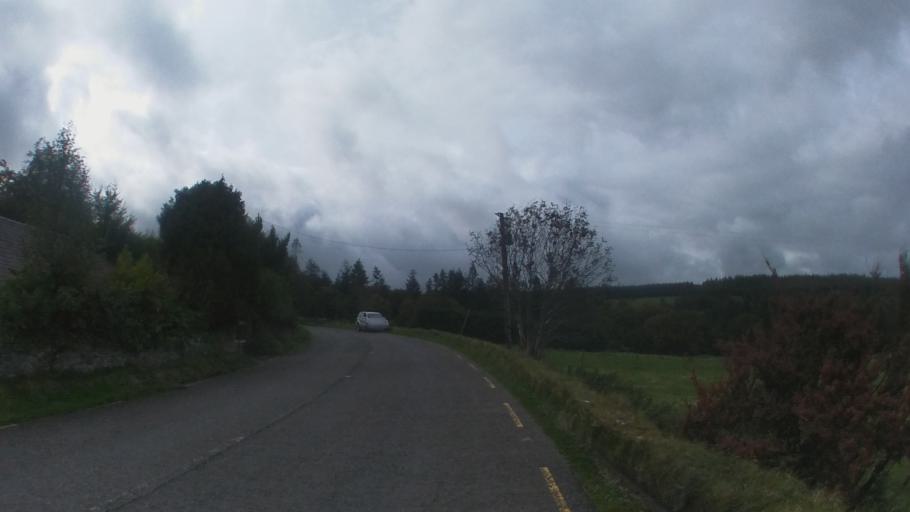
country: IE
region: Leinster
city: Ballyboden
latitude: 53.2422
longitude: -6.3132
